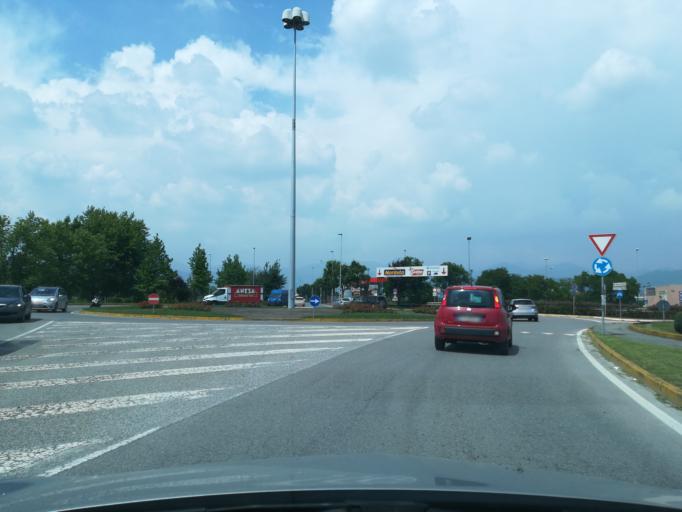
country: IT
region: Lombardy
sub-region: Provincia di Bergamo
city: Seriate
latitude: 45.6796
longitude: 9.7428
